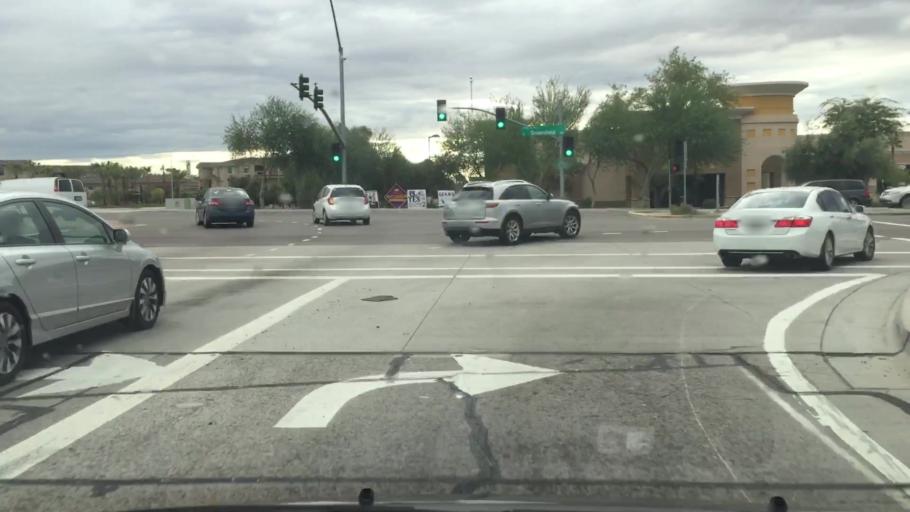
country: US
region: Arizona
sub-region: Maricopa County
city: Gilbert
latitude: 33.3845
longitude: -111.7378
